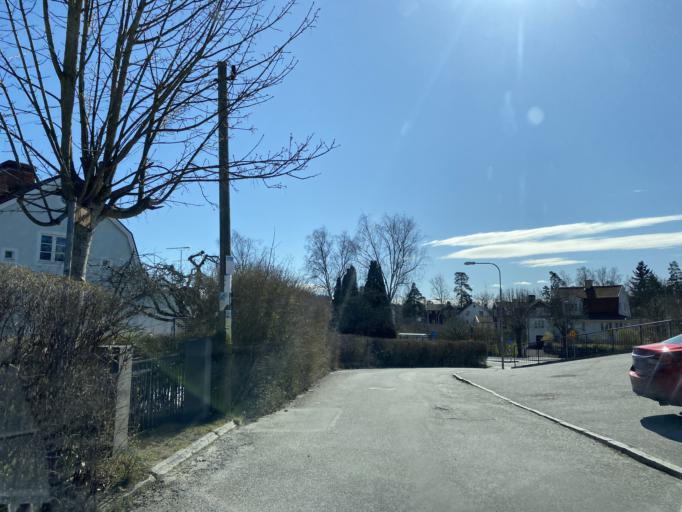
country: SE
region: Stockholm
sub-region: Stockholms Kommun
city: Arsta
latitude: 59.2806
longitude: 18.0565
